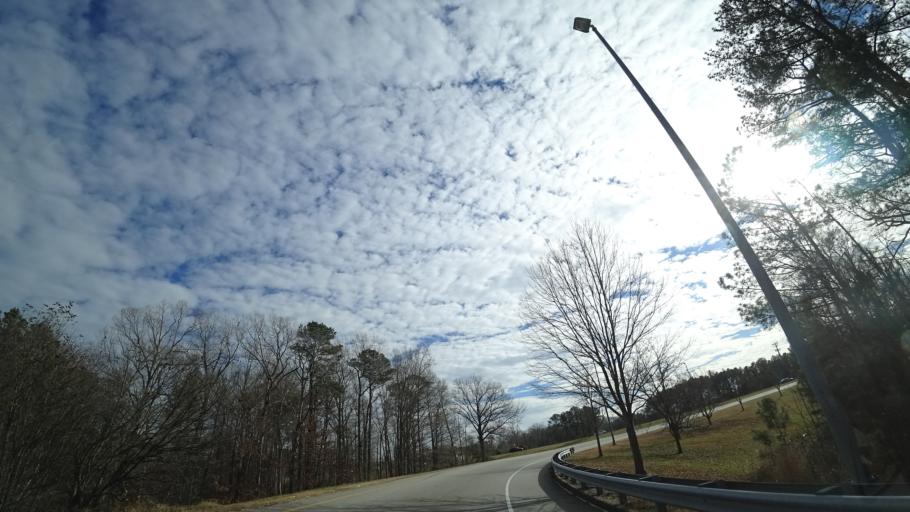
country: US
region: Virginia
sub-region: City of Poquoson
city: Poquoson
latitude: 37.1113
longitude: -76.4765
